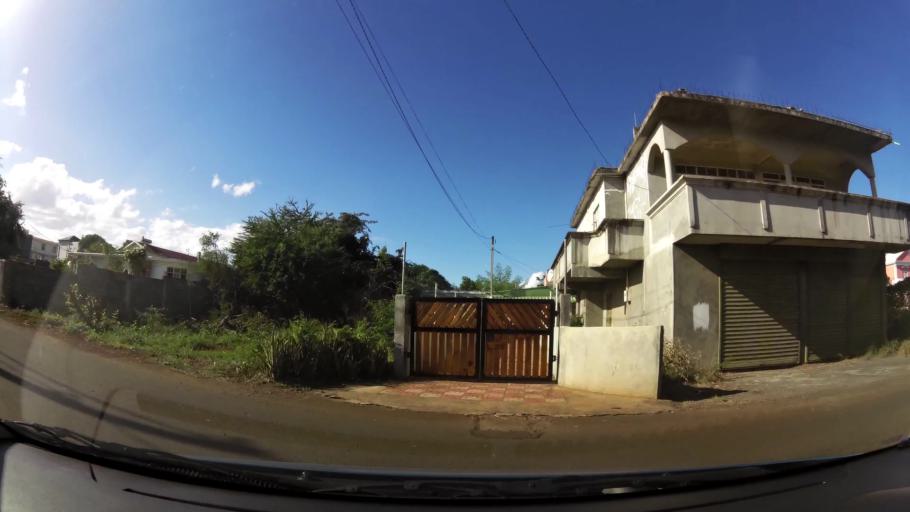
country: MU
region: Black River
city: Albion
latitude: -20.1996
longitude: 57.4124
